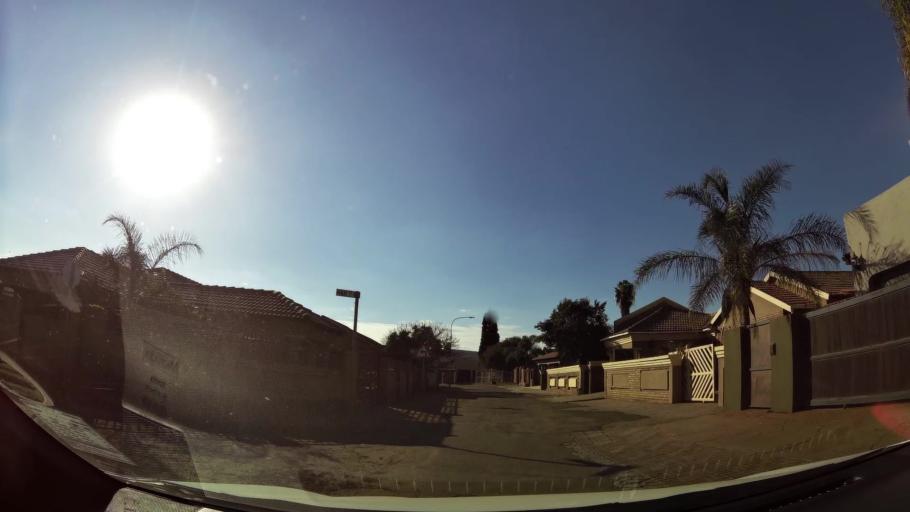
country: ZA
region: Gauteng
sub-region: City of Tshwane Metropolitan Municipality
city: Cullinan
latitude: -25.7131
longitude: 28.3892
